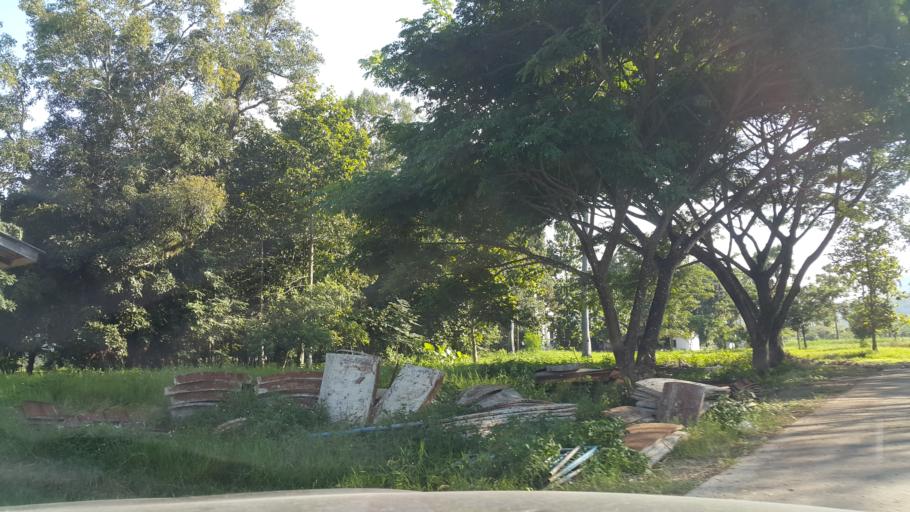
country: TH
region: Chiang Mai
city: Mae On
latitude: 18.7244
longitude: 99.2015
